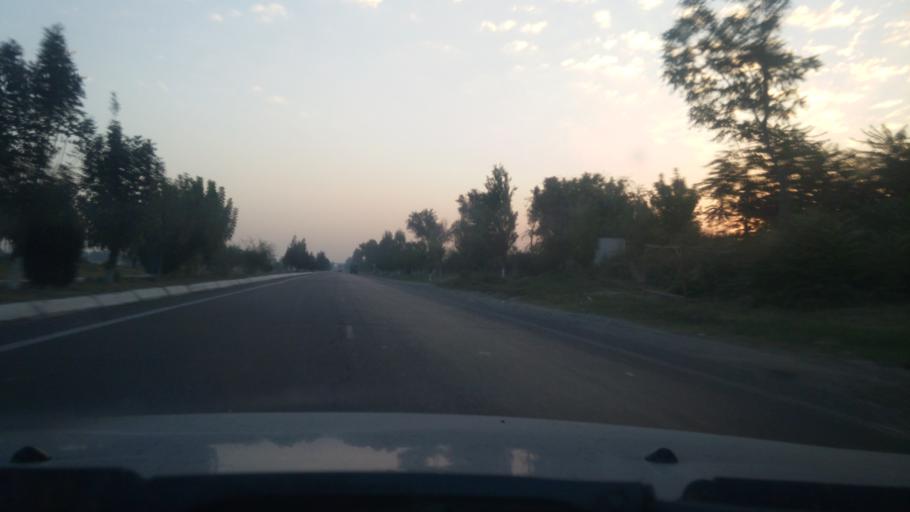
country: UZ
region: Toshkent
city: Zafar
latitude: 41.0024
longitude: 68.8244
